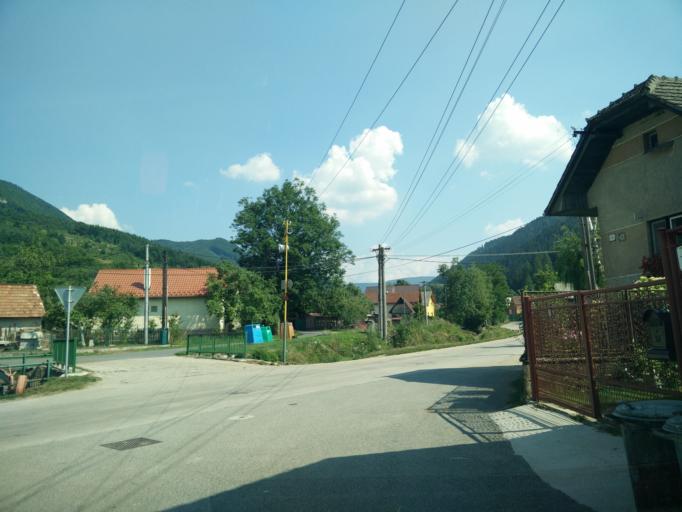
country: SK
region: Zilinsky
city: Rajec
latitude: 49.0424
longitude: 18.6413
